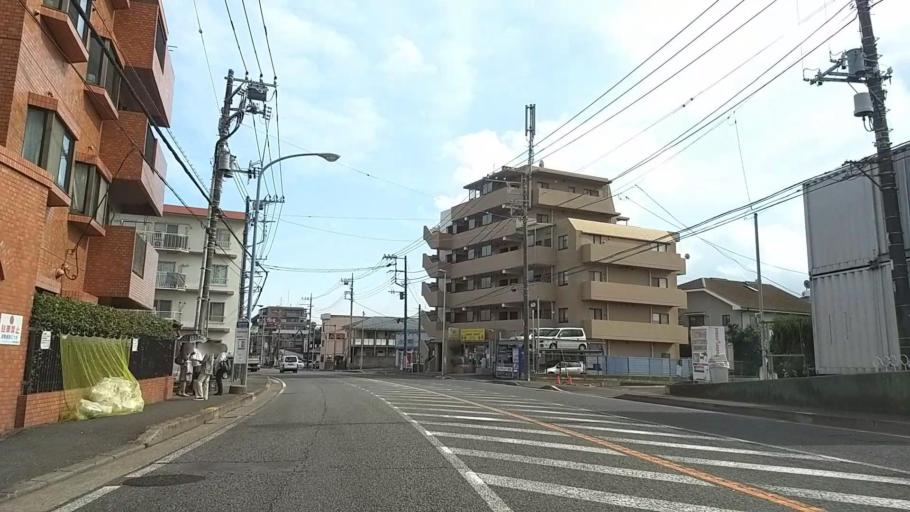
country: JP
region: Kanagawa
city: Yokohama
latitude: 35.5108
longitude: 139.5852
